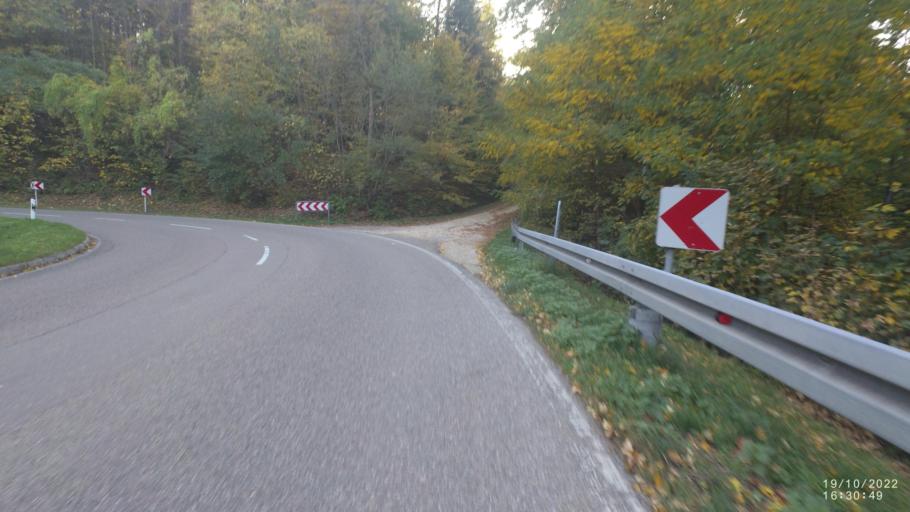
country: DE
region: Baden-Wuerttemberg
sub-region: Regierungsbezirk Stuttgart
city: Boll
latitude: 48.6286
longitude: 9.6069
